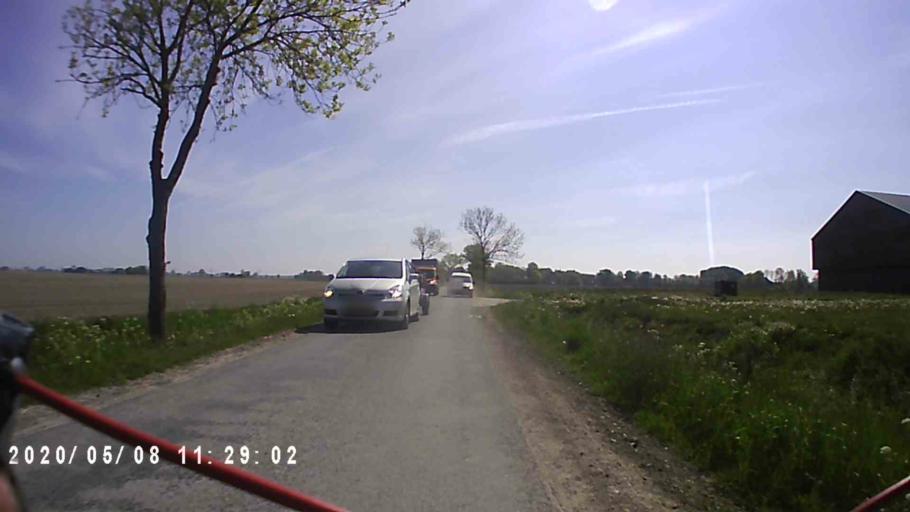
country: NL
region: Groningen
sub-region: Gemeente Bedum
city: Bedum
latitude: 53.3467
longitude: 6.6984
